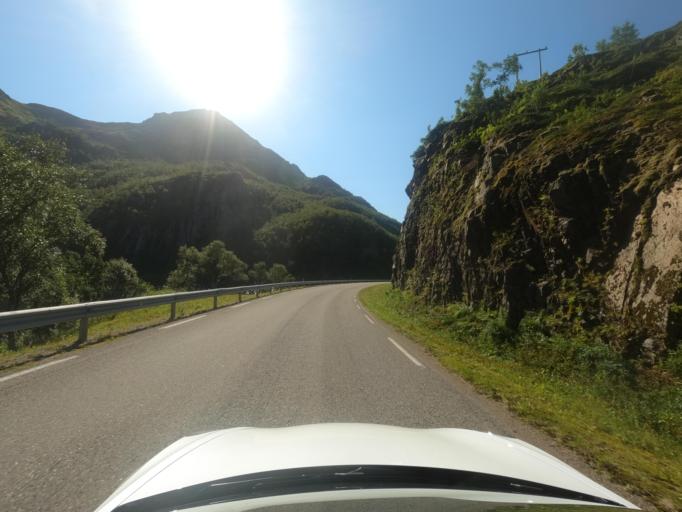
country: NO
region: Nordland
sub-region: Hadsel
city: Stokmarknes
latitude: 68.4519
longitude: 15.2049
